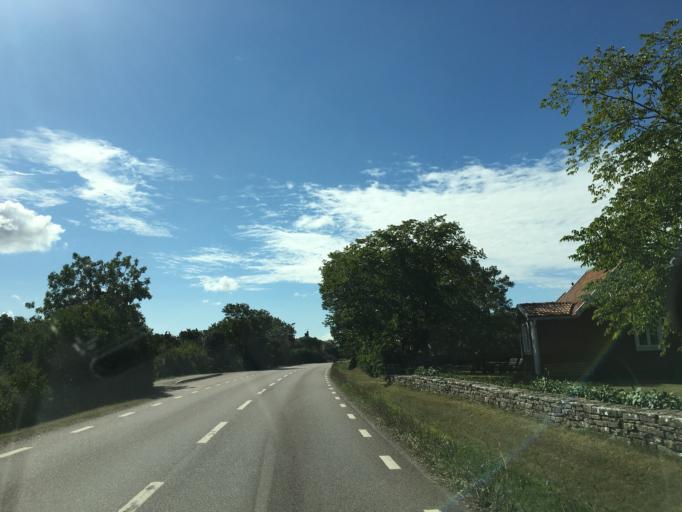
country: SE
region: Kalmar
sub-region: Morbylanga Kommun
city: Moerbylanga
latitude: 56.5400
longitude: 16.4455
